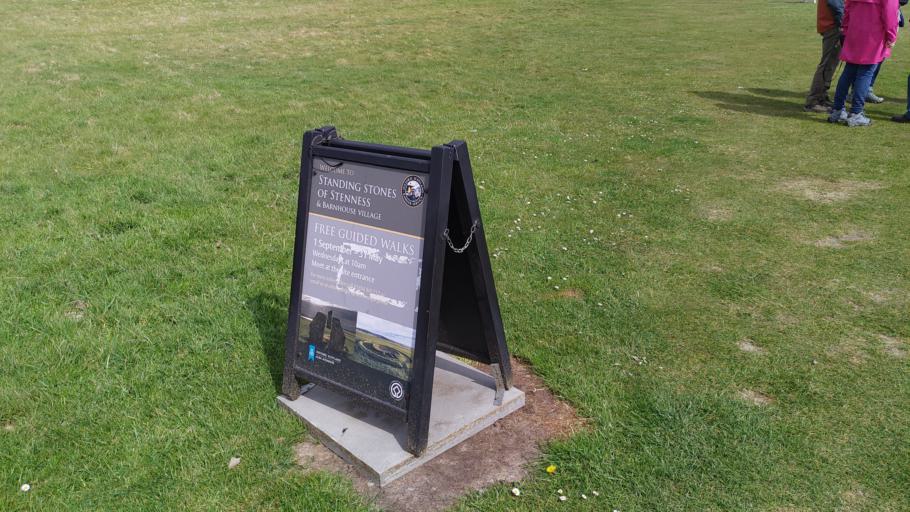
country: GB
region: Scotland
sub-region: Orkney Islands
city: Stromness
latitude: 58.9928
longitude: -3.2076
